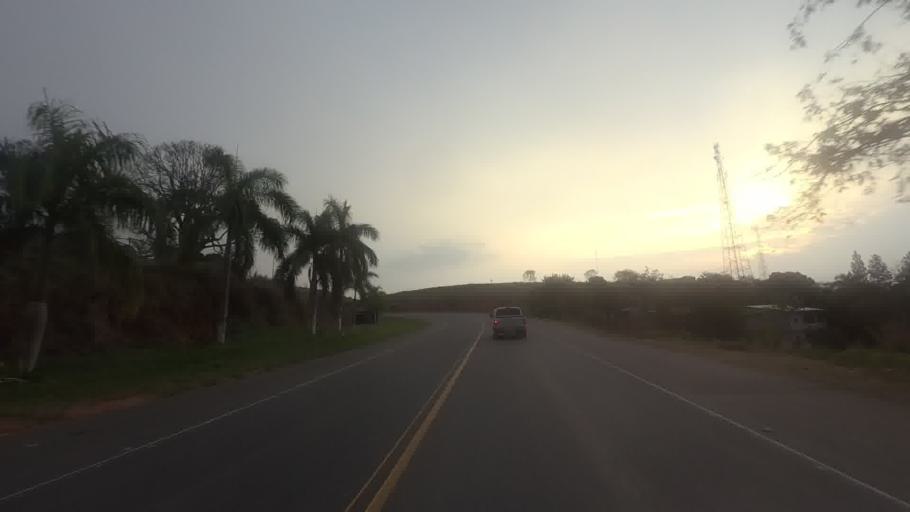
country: BR
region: Rio de Janeiro
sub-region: Carmo
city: Carmo
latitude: -21.7755
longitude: -42.5361
